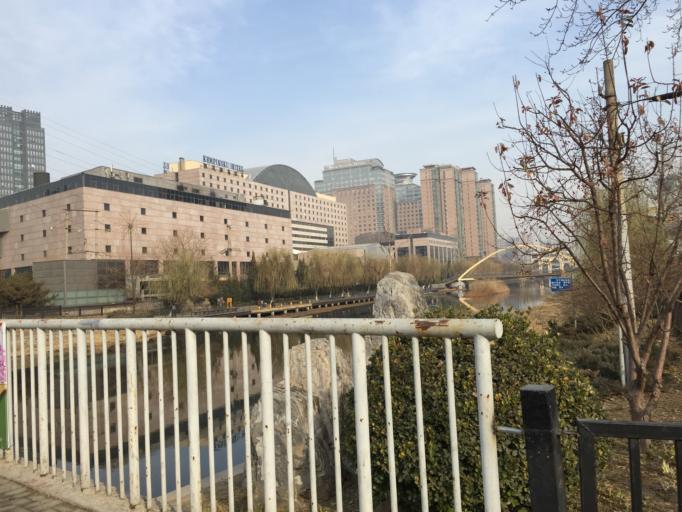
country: CN
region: Beijing
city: Chaowai
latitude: 39.9461
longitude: 116.4561
